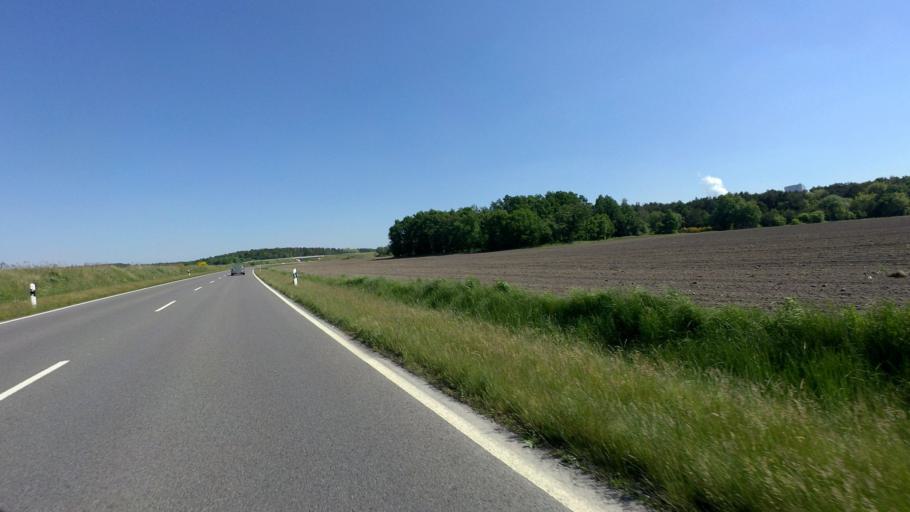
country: DE
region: Brandenburg
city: Spremberg
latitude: 51.5333
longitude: 14.3206
